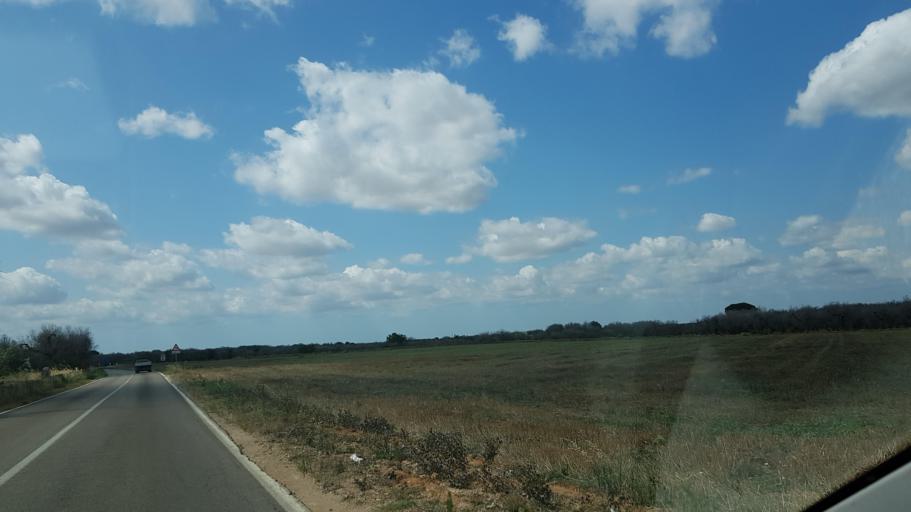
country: IT
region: Apulia
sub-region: Provincia di Brindisi
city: Torchiarolo
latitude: 40.4673
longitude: 18.0597
